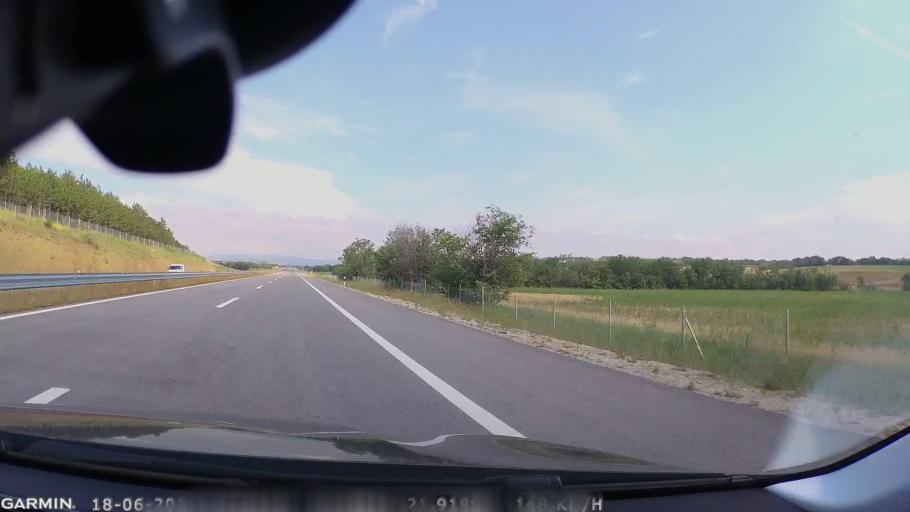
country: MK
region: Sveti Nikole
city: Sveti Nikole
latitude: 41.8995
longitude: 21.9169
